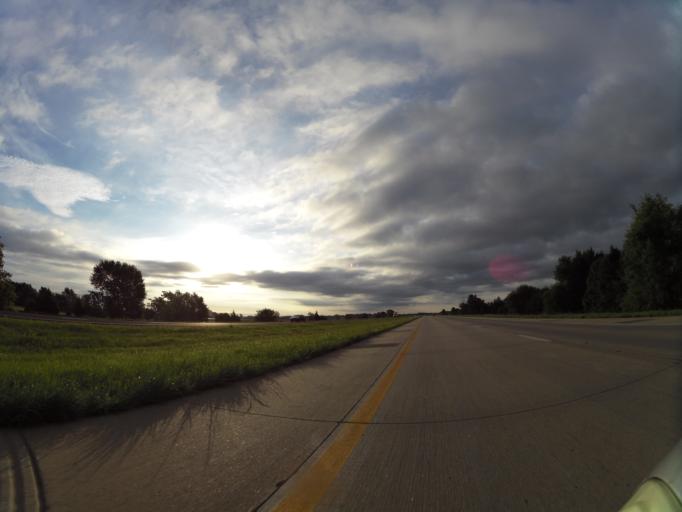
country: US
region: Kansas
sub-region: Reno County
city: Haven
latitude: 37.8813
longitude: -97.7184
